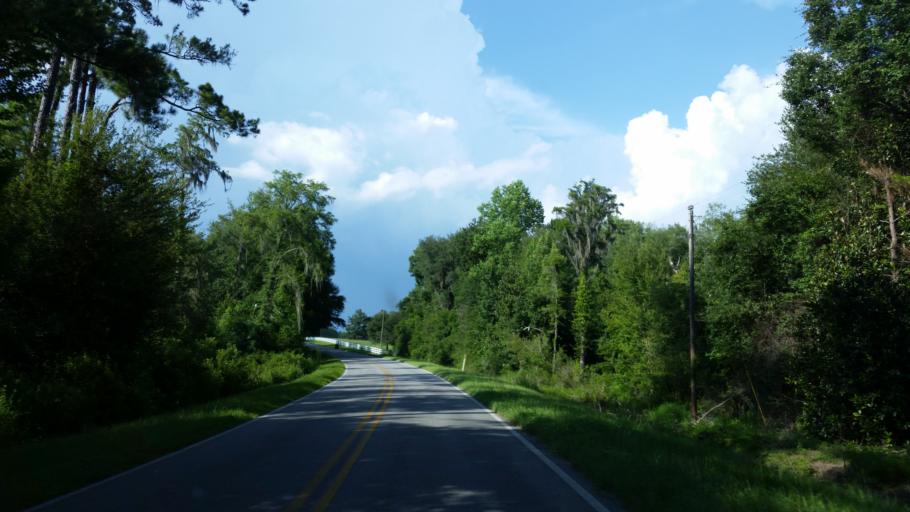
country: US
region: Georgia
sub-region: Lowndes County
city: Hahira
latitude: 30.9519
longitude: -83.4090
